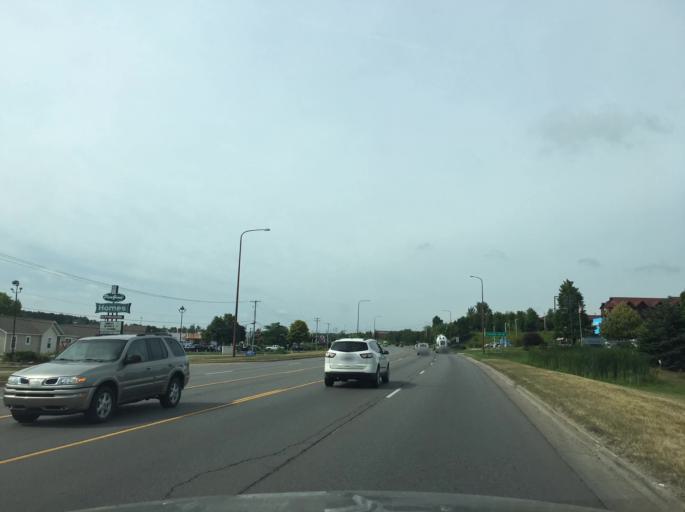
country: US
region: Michigan
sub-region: Grand Traverse County
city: Traverse City
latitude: 44.7413
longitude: -85.6433
